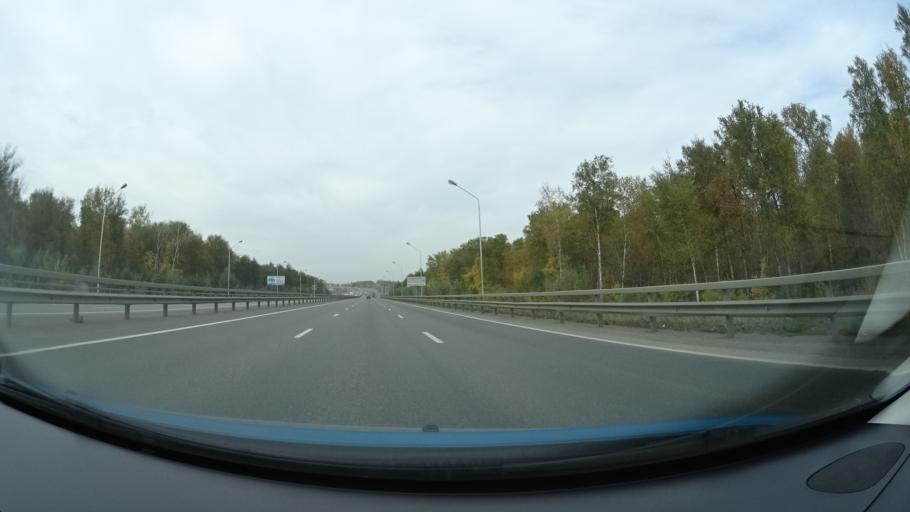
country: RU
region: Bashkortostan
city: Avdon
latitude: 54.6732
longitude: 55.8255
